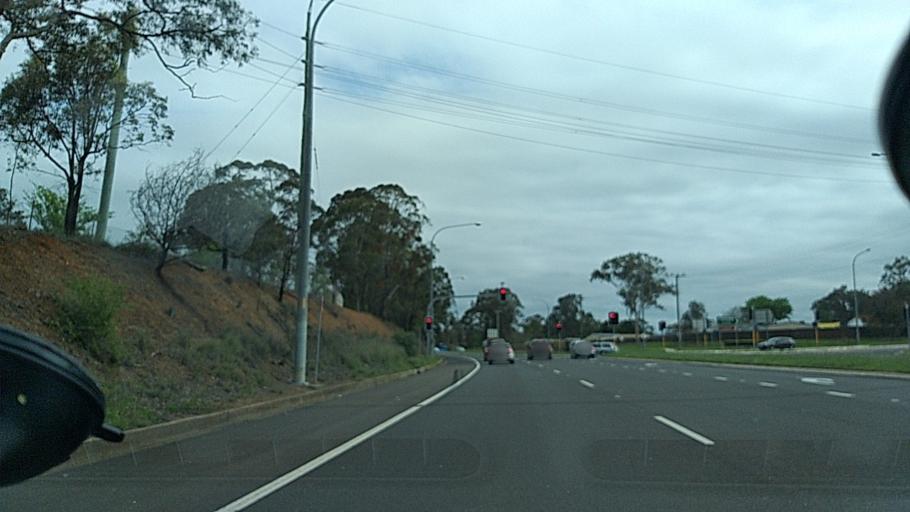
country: AU
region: New South Wales
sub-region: Camden
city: Camden South
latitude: -34.0754
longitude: 150.6955
